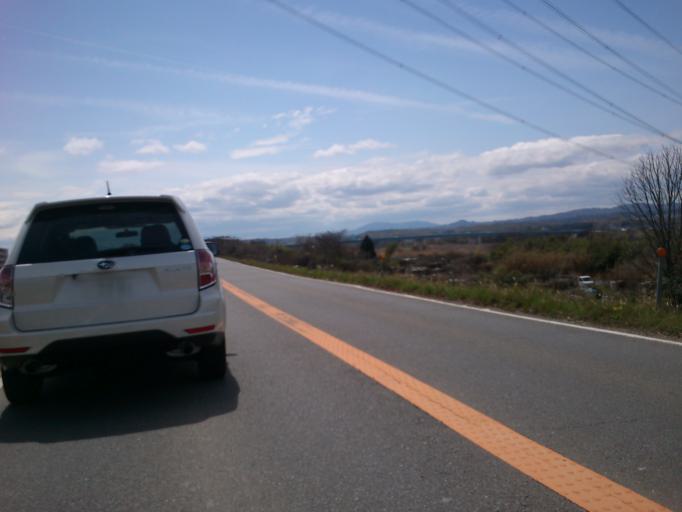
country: JP
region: Kyoto
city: Tanabe
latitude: 34.8045
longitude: 135.8046
